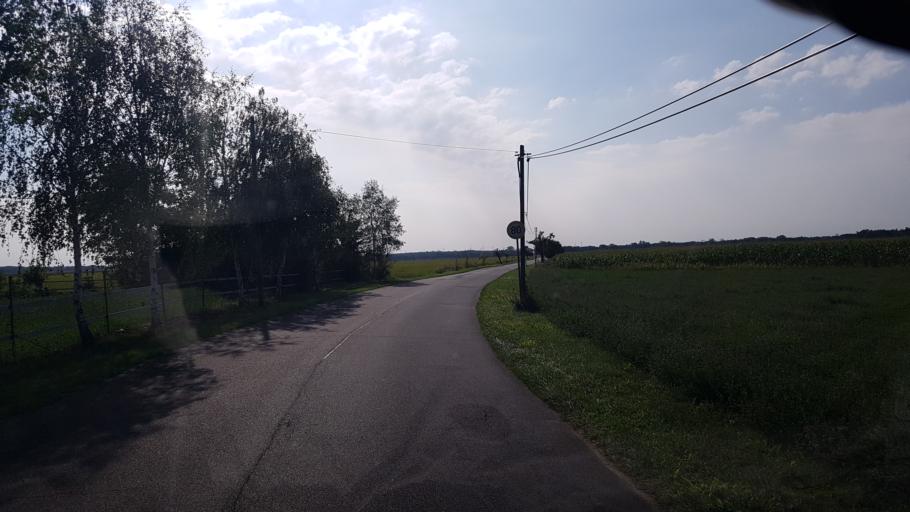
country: DE
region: Brandenburg
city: Luebben
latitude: 51.8797
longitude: 13.8457
